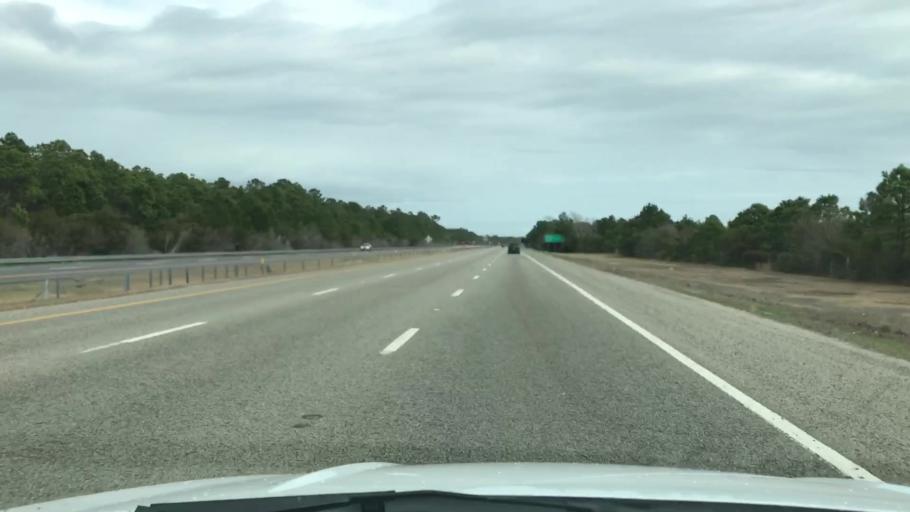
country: US
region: South Carolina
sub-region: Horry County
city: Socastee
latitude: 33.7148
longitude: -79.0034
